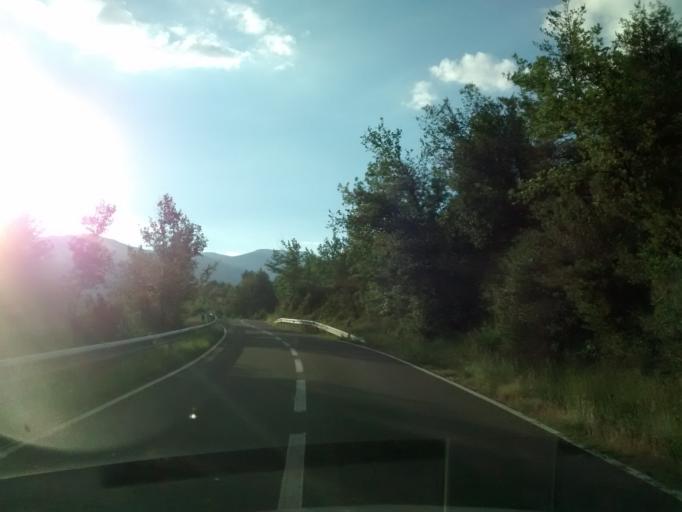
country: ES
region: Aragon
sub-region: Provincia de Huesca
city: Boltana
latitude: 42.4717
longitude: -0.0015
